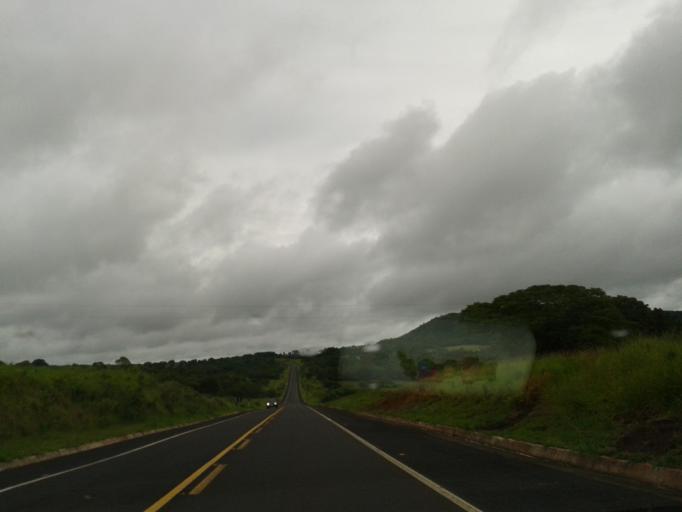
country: BR
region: Minas Gerais
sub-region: Santa Vitoria
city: Santa Vitoria
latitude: -19.2230
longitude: -50.0202
